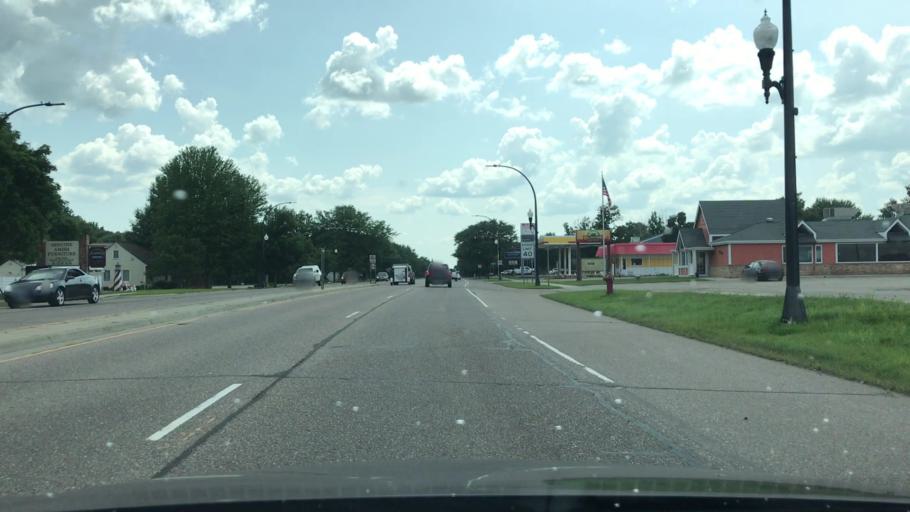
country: US
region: Minnesota
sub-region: Nicollet County
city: Saint Peter
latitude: 44.3331
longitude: -93.9496
